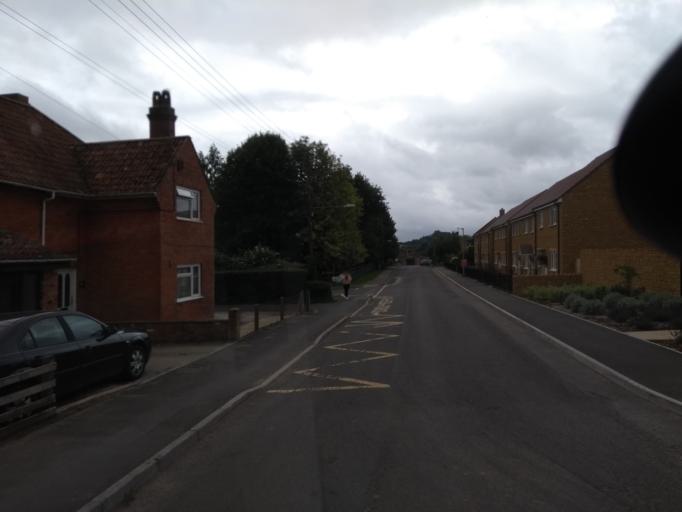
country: GB
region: England
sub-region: Somerset
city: Stoke-sub-Hamdon
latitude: 50.9425
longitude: -2.7562
